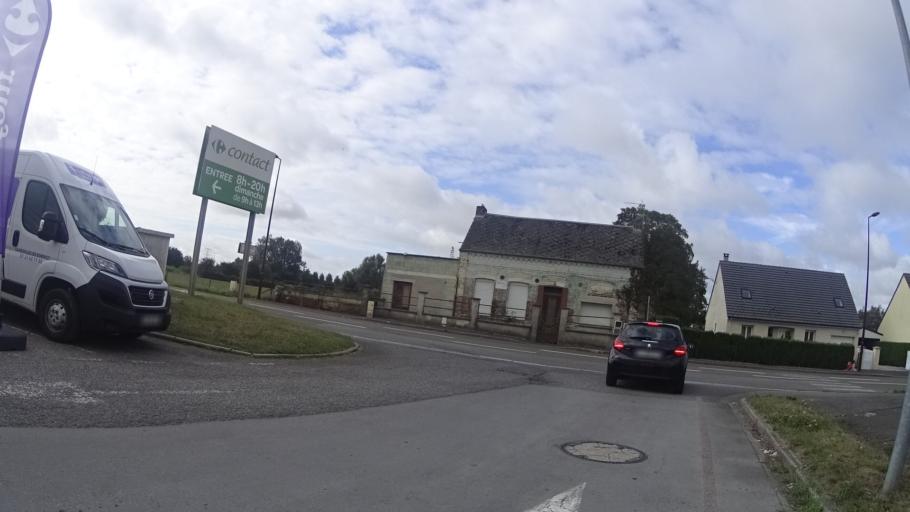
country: FR
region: Picardie
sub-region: Departement de l'Aisne
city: Boue
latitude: 50.0016
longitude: 3.6857
